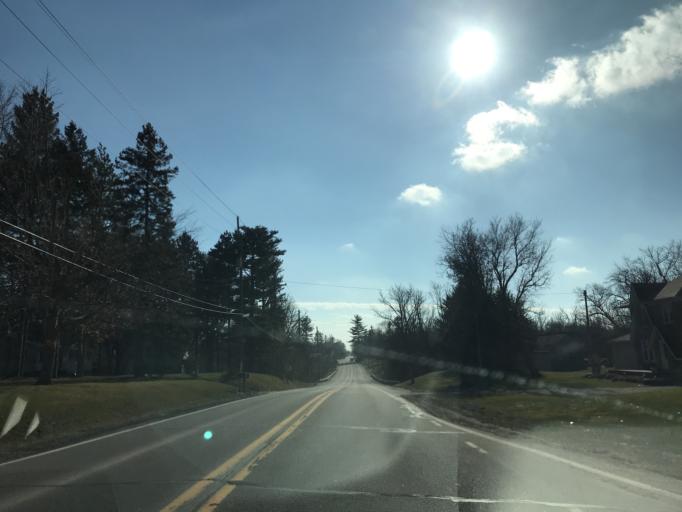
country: US
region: Michigan
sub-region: Oakland County
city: South Lyon
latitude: 42.4548
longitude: -83.6962
